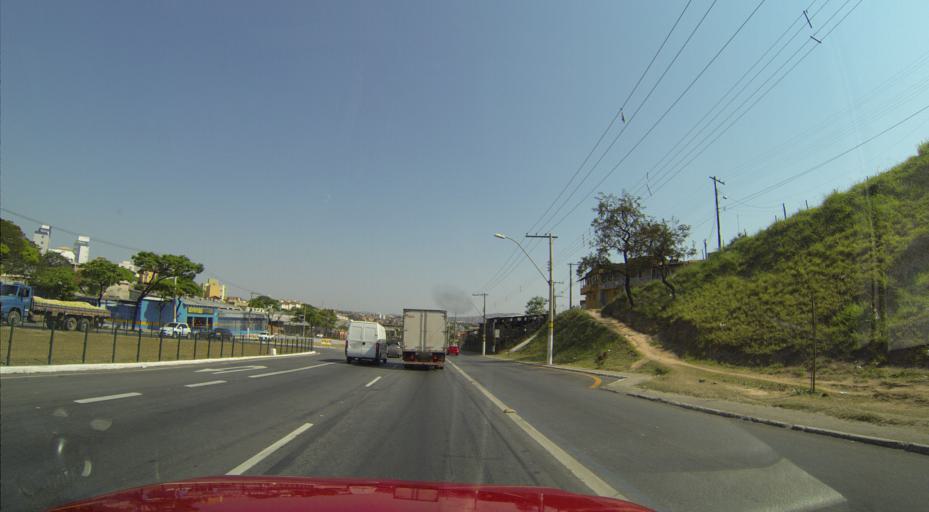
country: BR
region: Minas Gerais
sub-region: Belo Horizonte
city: Belo Horizonte
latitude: -19.8424
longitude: -43.9343
